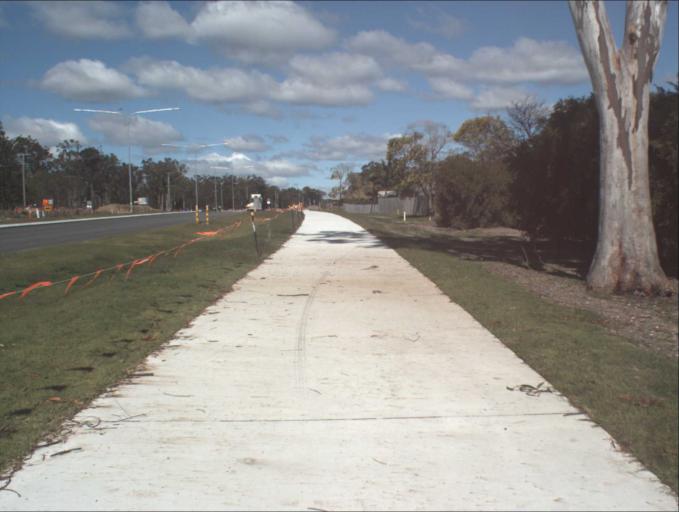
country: AU
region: Queensland
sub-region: Logan
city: Logan Reserve
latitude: -27.6981
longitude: 153.1005
